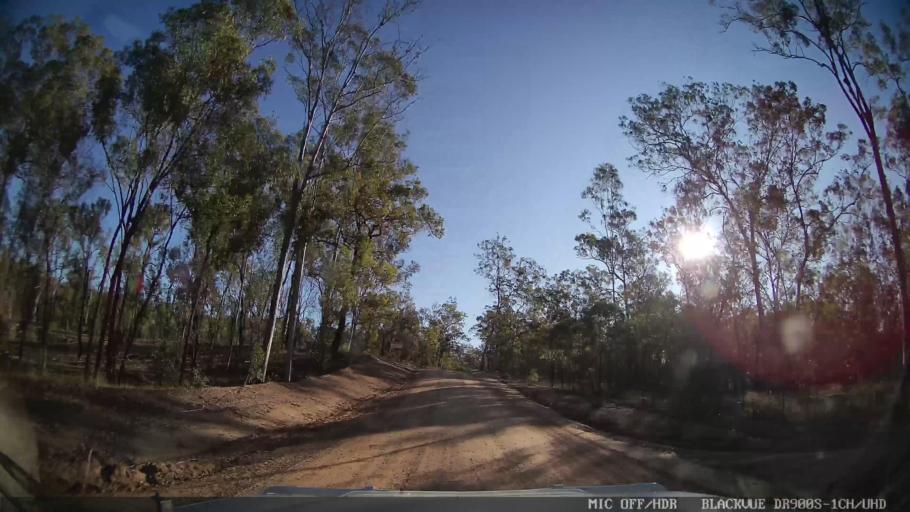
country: AU
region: Queensland
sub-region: Bundaberg
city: Sharon
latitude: -24.7362
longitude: 151.5197
